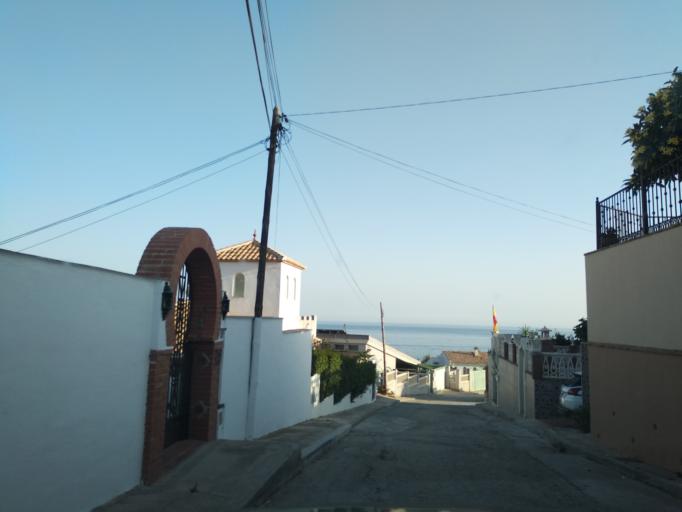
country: ES
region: Andalusia
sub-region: Provincia de Malaga
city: Iznate
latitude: 36.7187
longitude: -4.1898
